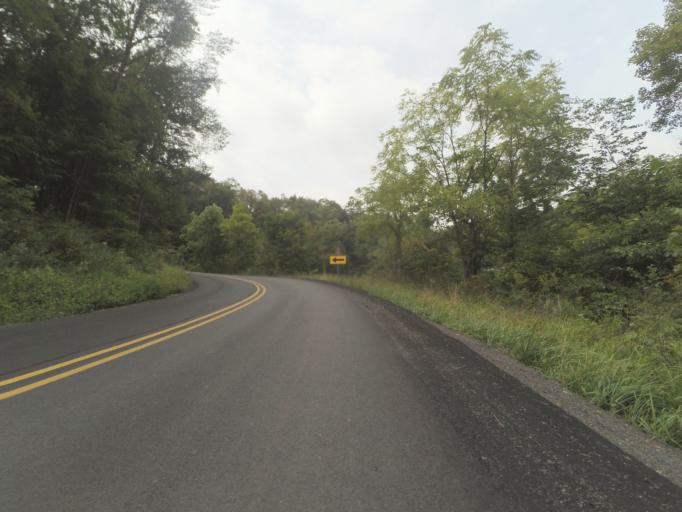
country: US
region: Pennsylvania
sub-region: Huntingdon County
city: McConnellstown
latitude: 40.5834
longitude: -78.1057
